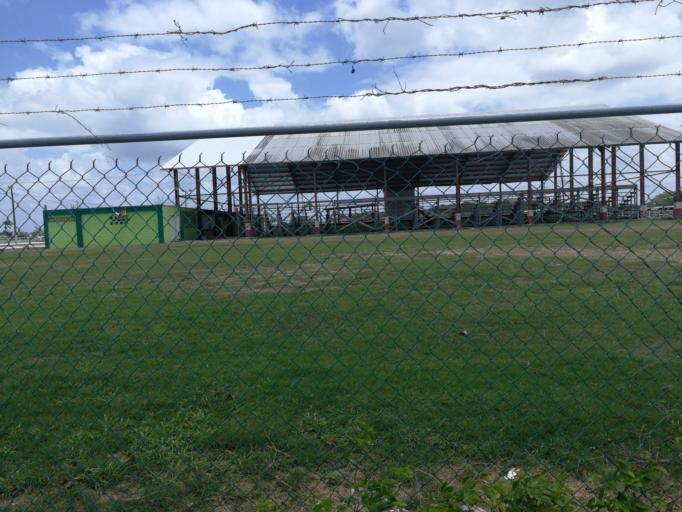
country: BZ
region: Orange Walk
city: Orange Walk
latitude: 18.0851
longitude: -88.5701
